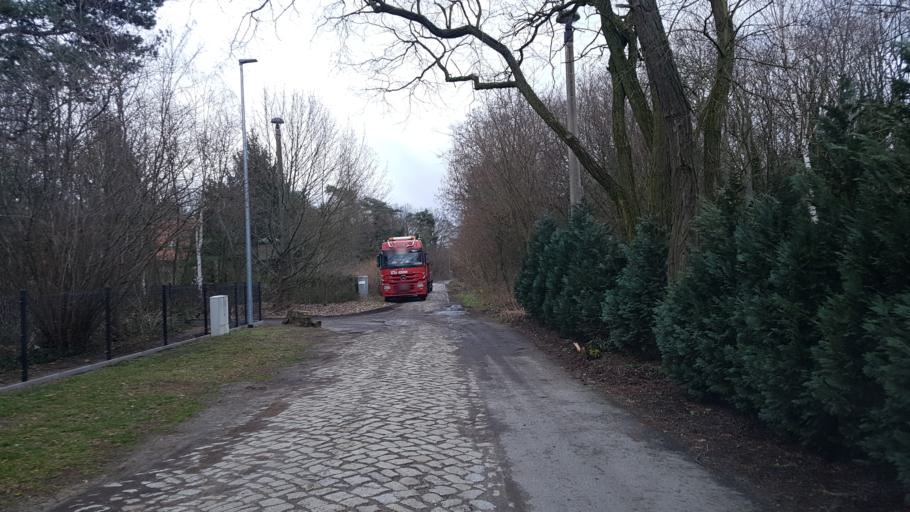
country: DE
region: Brandenburg
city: Plessa
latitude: 51.4737
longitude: 13.5807
